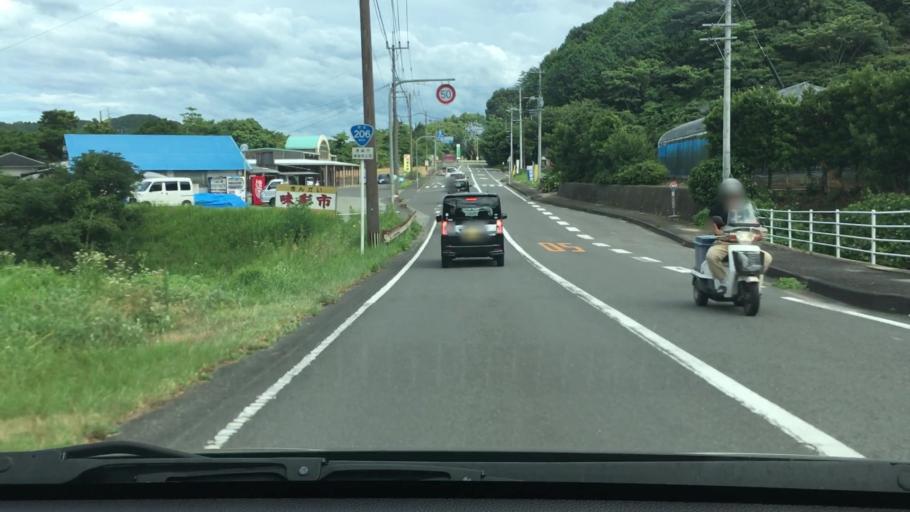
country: JP
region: Nagasaki
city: Togitsu
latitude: 32.9282
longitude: 129.7836
